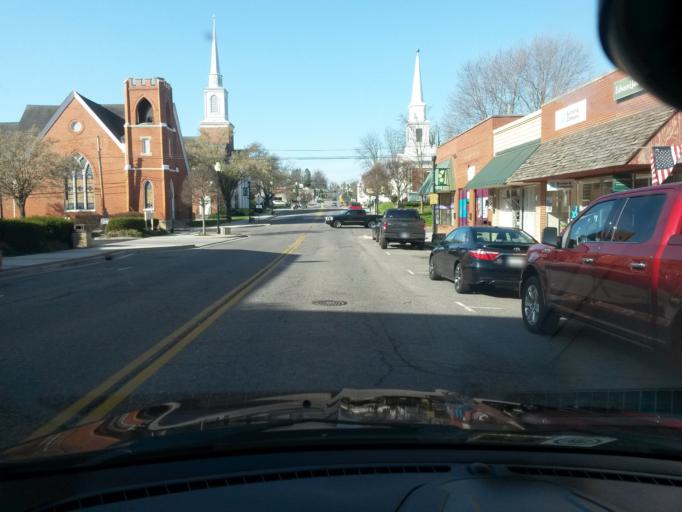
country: US
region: Virginia
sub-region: Montgomery County
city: Christiansburg
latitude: 37.1291
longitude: -80.4098
